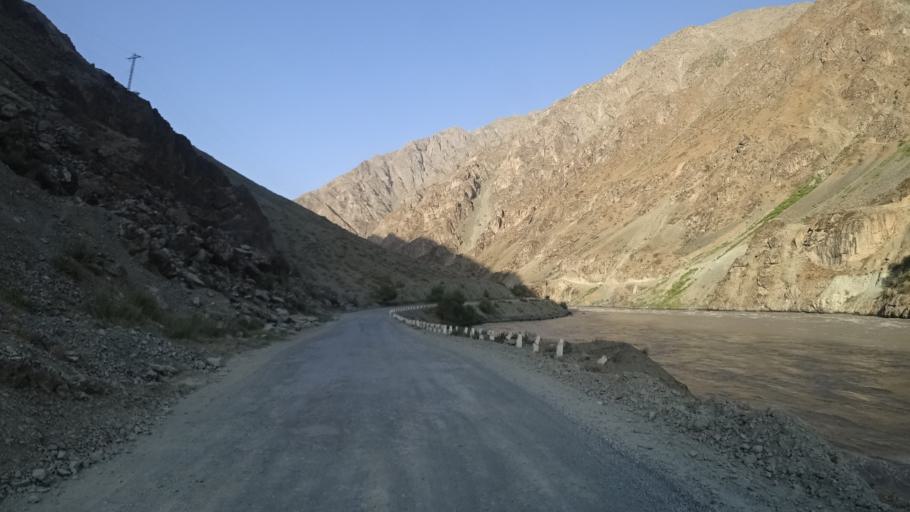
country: TJ
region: Gorno-Badakhshan
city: Qalaikhumb
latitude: 38.4168
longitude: 70.7306
